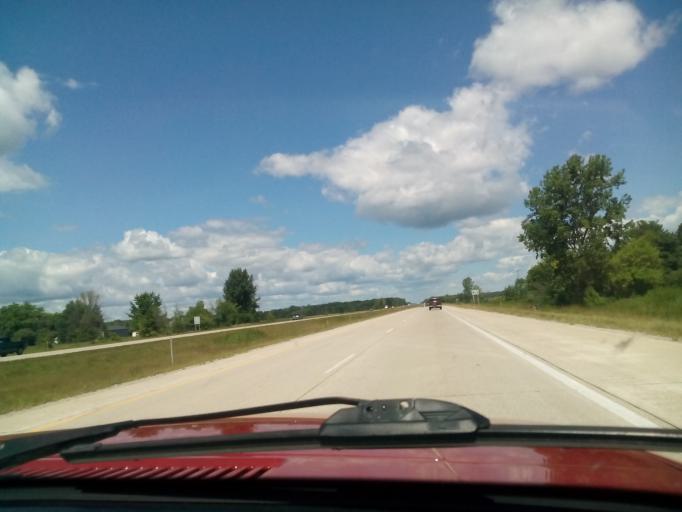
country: US
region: Michigan
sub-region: Bay County
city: Pinconning
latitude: 43.8093
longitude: -84.0205
